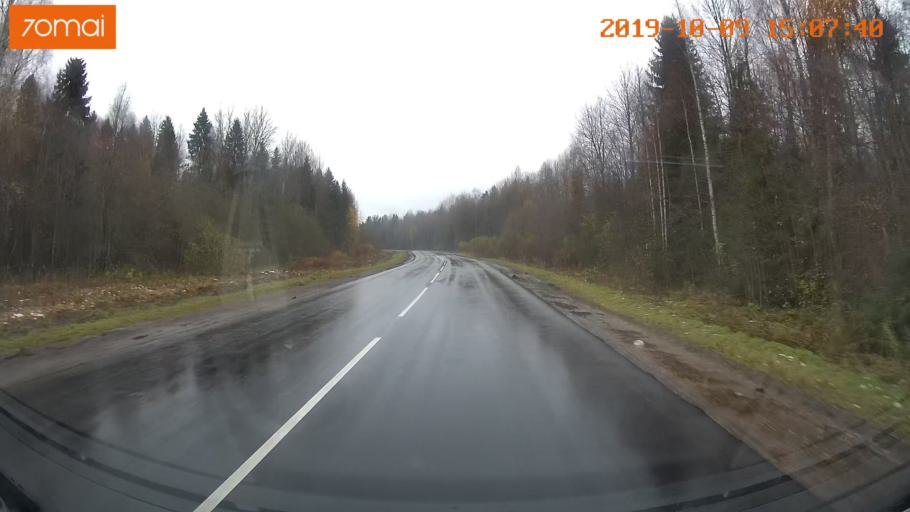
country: RU
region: Kostroma
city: Susanino
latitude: 58.2163
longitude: 41.6478
